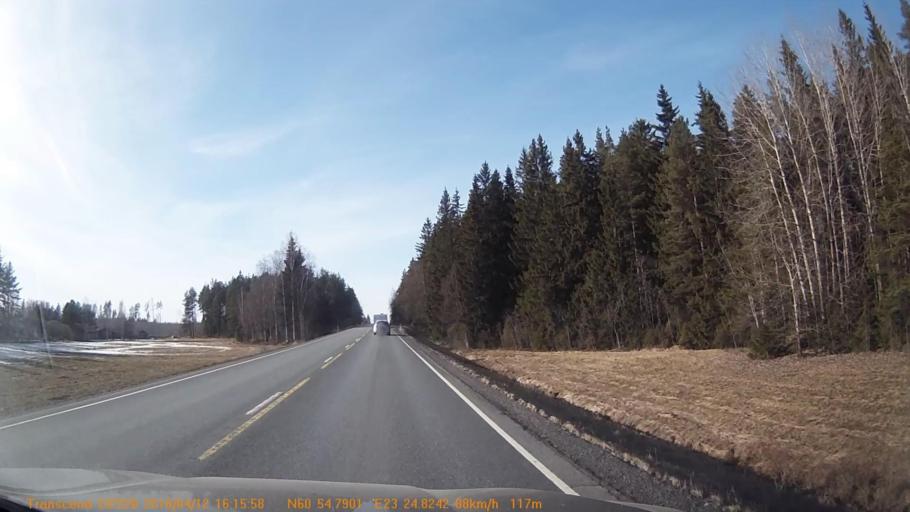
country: FI
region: Haeme
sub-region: Forssa
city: Humppila
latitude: 60.9133
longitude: 23.4134
